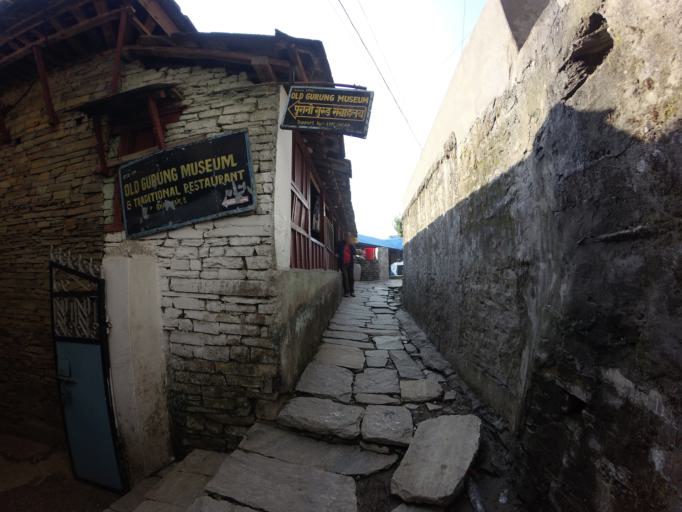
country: NP
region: Western Region
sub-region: Dhawalagiri Zone
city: Chitre
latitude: 28.3771
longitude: 83.8088
